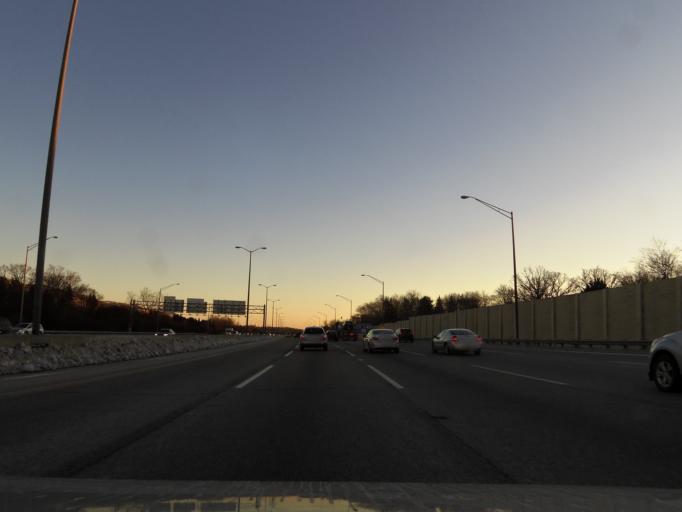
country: US
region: Illinois
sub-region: DuPage County
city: Oak Brook
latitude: 41.8400
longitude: -87.9199
